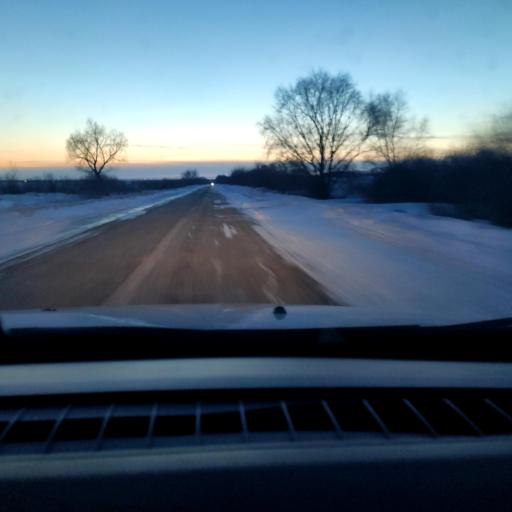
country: RU
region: Samara
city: Georgiyevka
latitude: 53.3375
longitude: 50.9466
